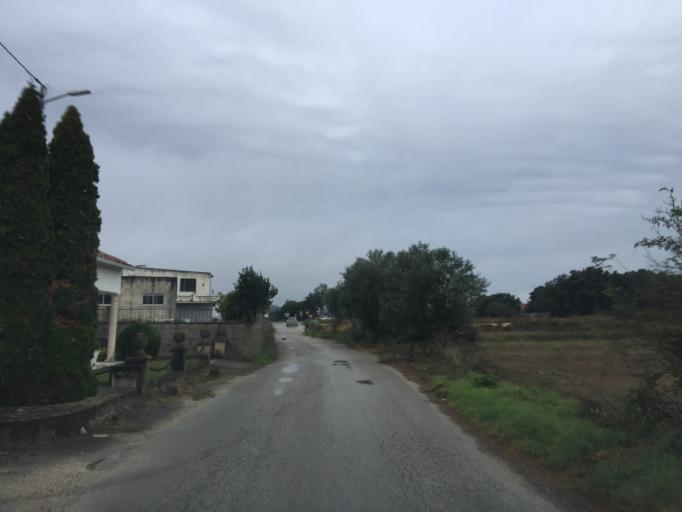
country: PT
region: Leiria
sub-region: Alcobaca
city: Benedita
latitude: 39.4345
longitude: -8.9549
